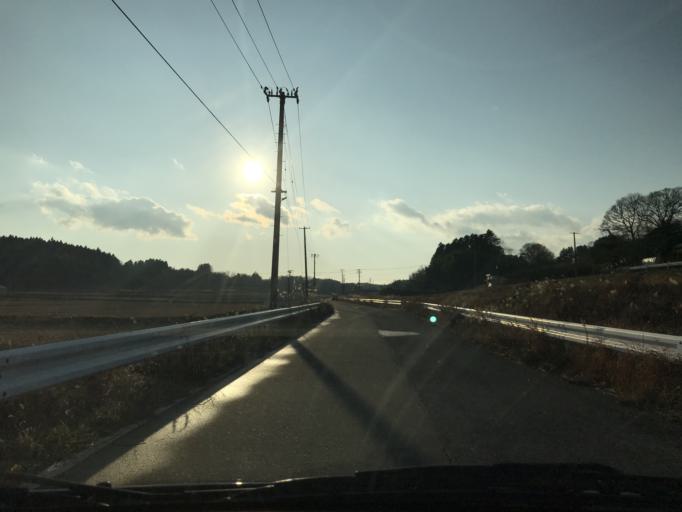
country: JP
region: Miyagi
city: Wakuya
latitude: 38.7028
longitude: 141.1204
